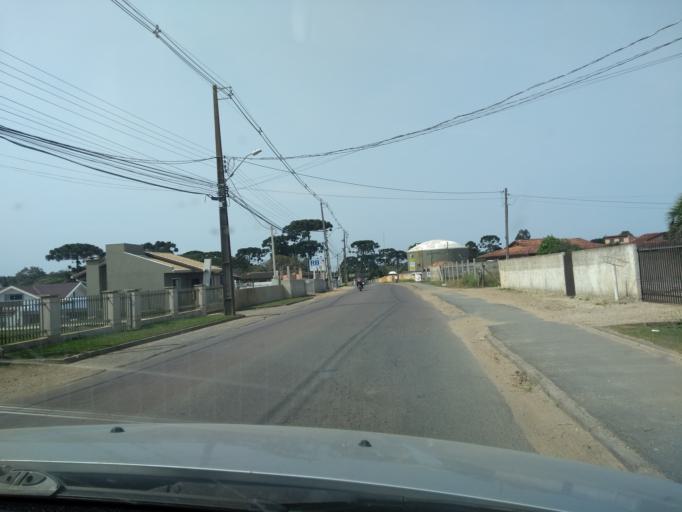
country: BR
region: Parana
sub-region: Araucaria
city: Araucaria
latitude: -25.6020
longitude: -49.3229
